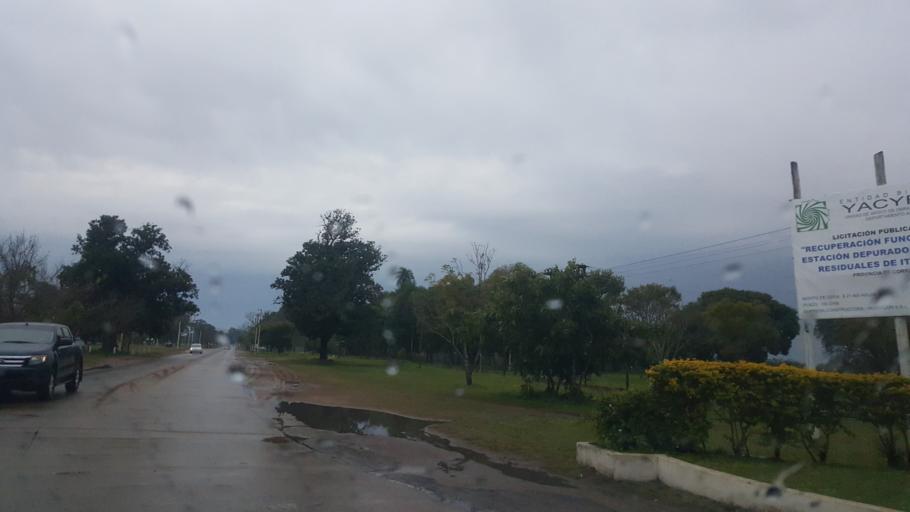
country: AR
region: Corrientes
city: Ituzaingo
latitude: -27.5914
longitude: -56.6874
